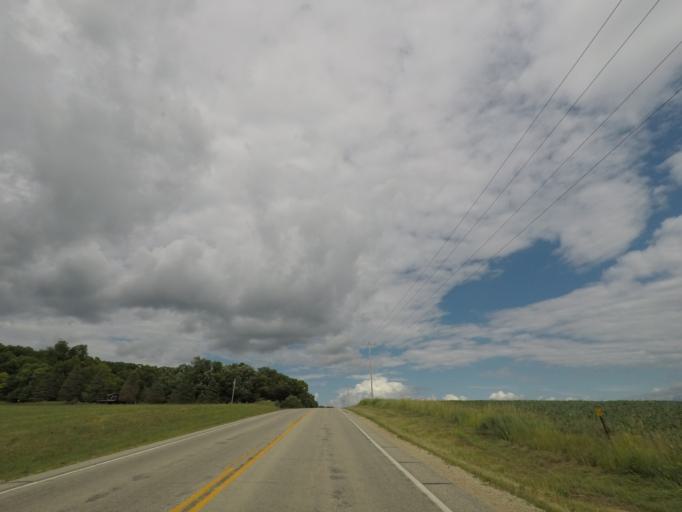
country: US
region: Wisconsin
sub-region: Dane County
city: Belleville
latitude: 42.8280
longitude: -89.4730
